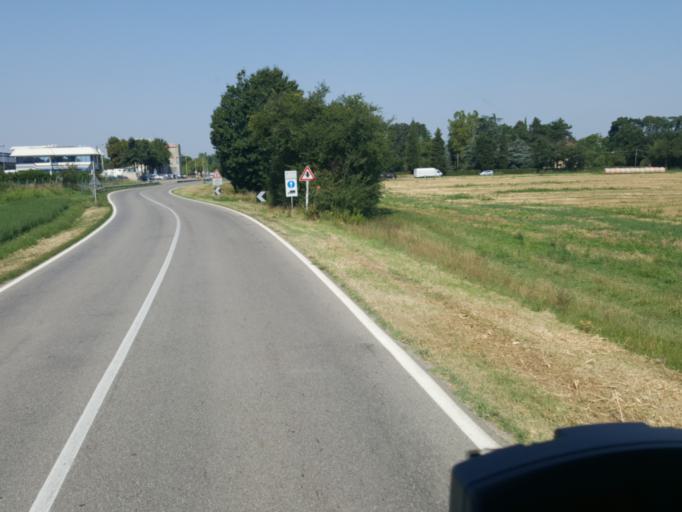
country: IT
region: Emilia-Romagna
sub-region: Provincia di Modena
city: Ca' di Sola
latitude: 44.5385
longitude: 10.9714
